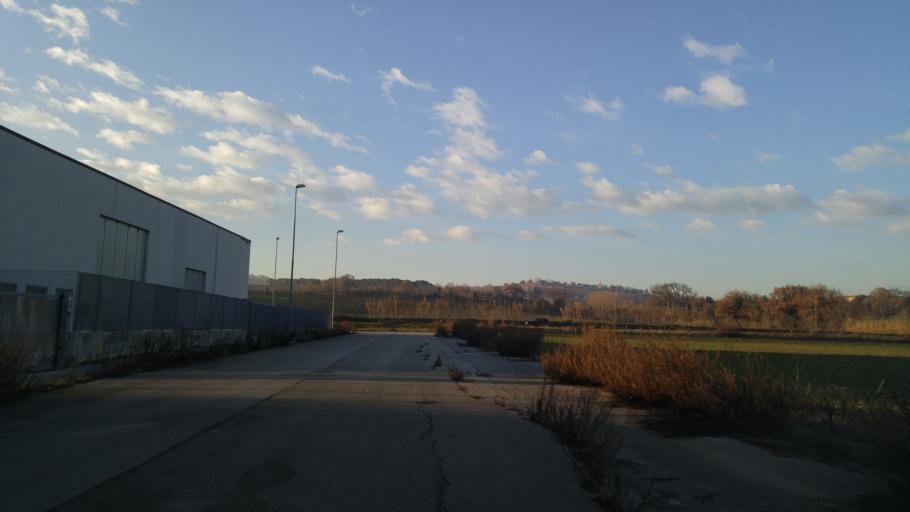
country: IT
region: The Marches
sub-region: Provincia di Ancona
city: Monterado
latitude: 43.7127
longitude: 13.0795
